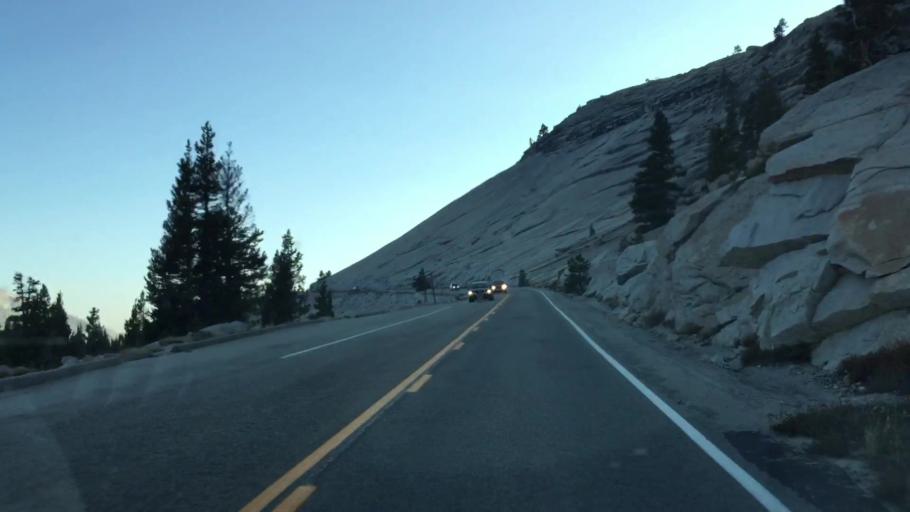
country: US
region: California
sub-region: Mariposa County
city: Yosemite Valley
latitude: 37.8175
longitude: -119.4799
